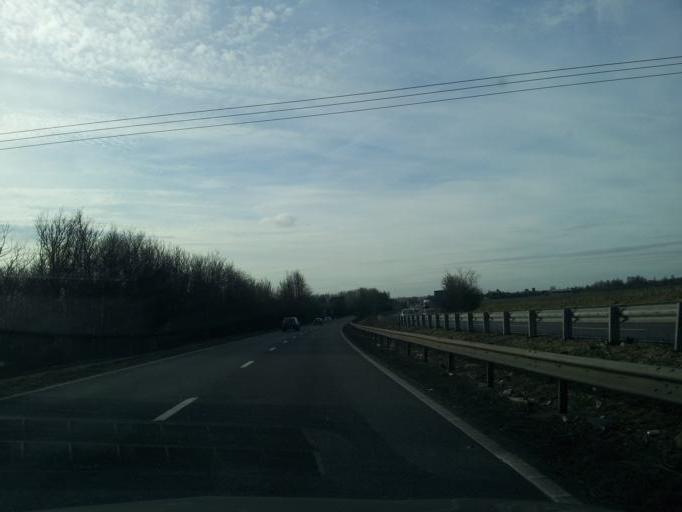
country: GB
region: England
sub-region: Cambridgeshire
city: Buckden
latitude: 52.2752
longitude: -0.2586
